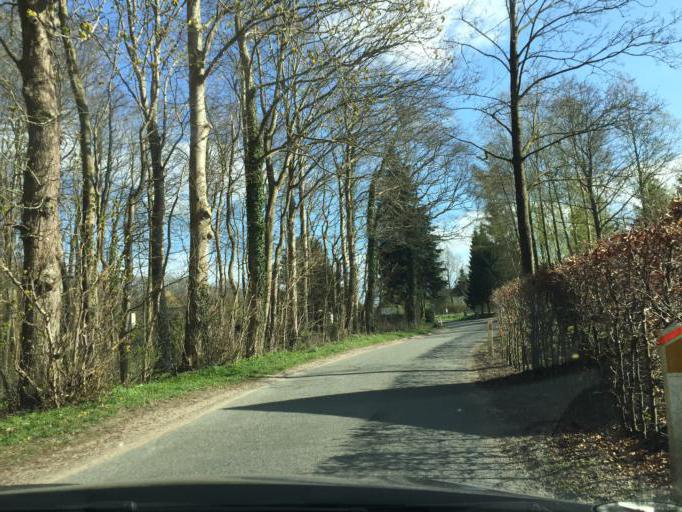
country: DK
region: South Denmark
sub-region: Faaborg-Midtfyn Kommune
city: Arslev
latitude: 55.2982
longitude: 10.4988
